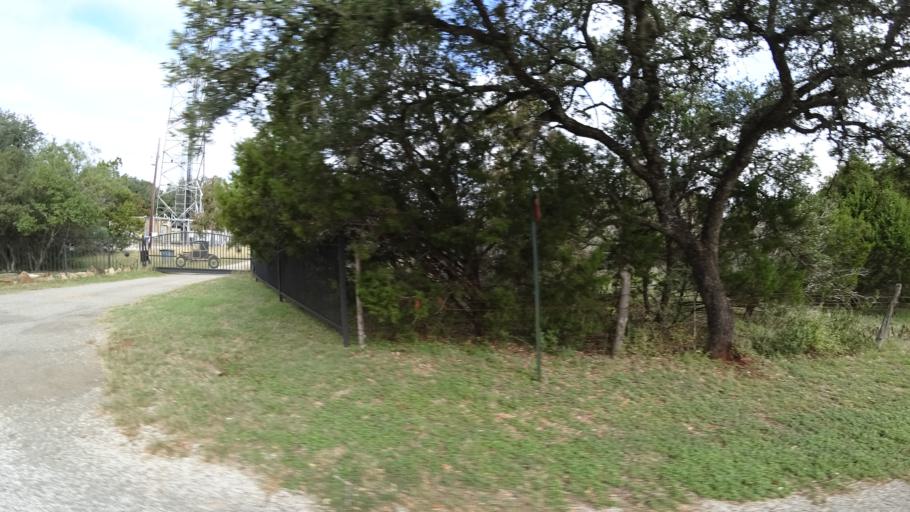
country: US
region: Texas
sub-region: Travis County
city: Shady Hollow
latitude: 30.1482
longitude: -97.8827
